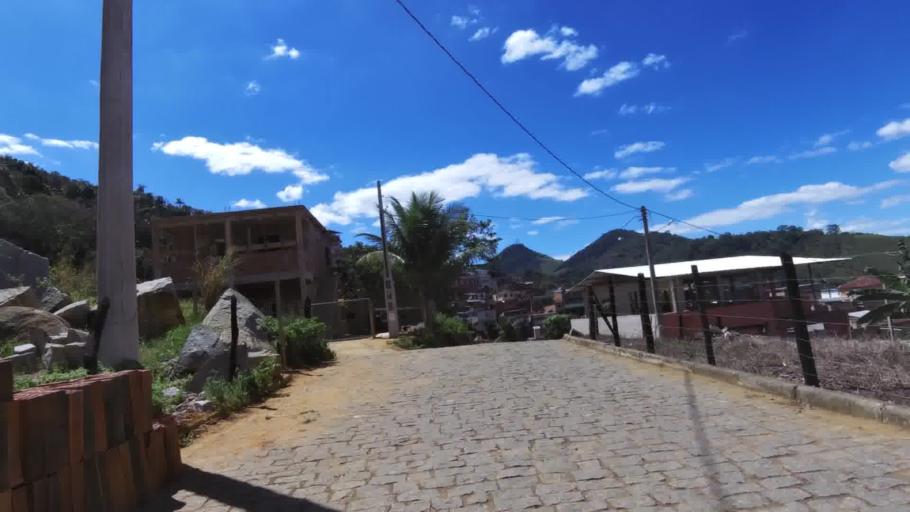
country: BR
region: Espirito Santo
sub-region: Rio Novo Do Sul
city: Rio Novo do Sul
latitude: -20.8635
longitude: -40.9390
